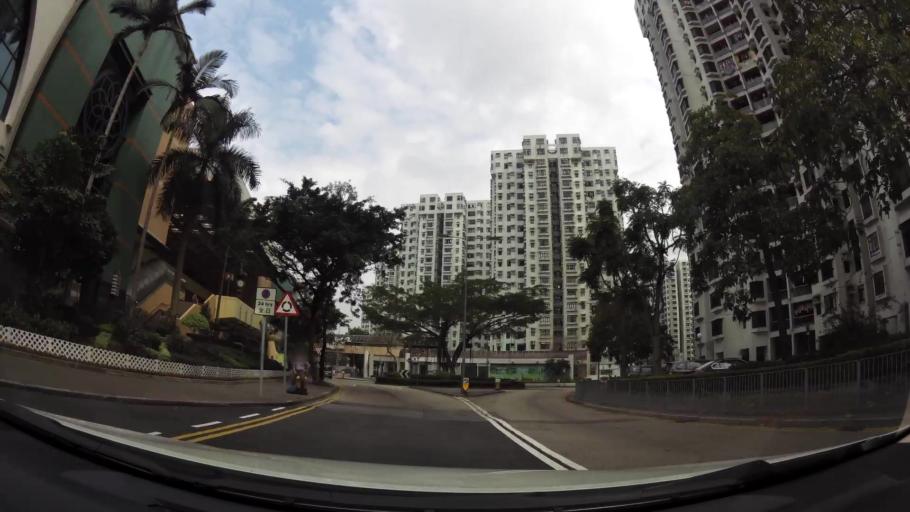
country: HK
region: Wanchai
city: Wan Chai
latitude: 22.2764
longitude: 114.2406
